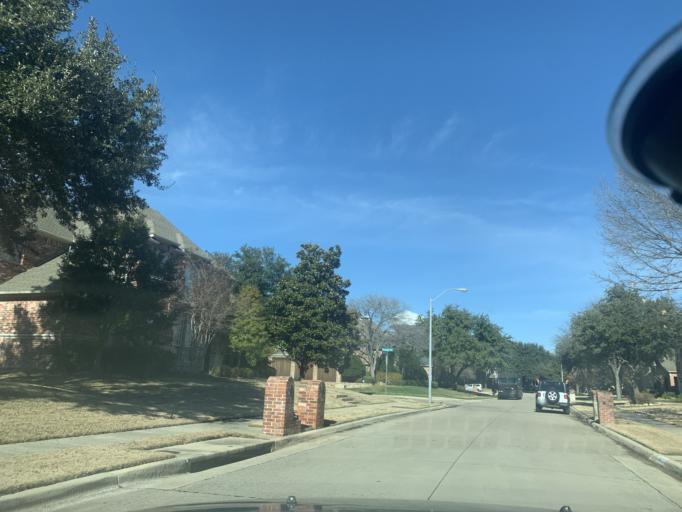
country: US
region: Texas
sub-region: Denton County
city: The Colony
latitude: 33.0536
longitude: -96.8206
